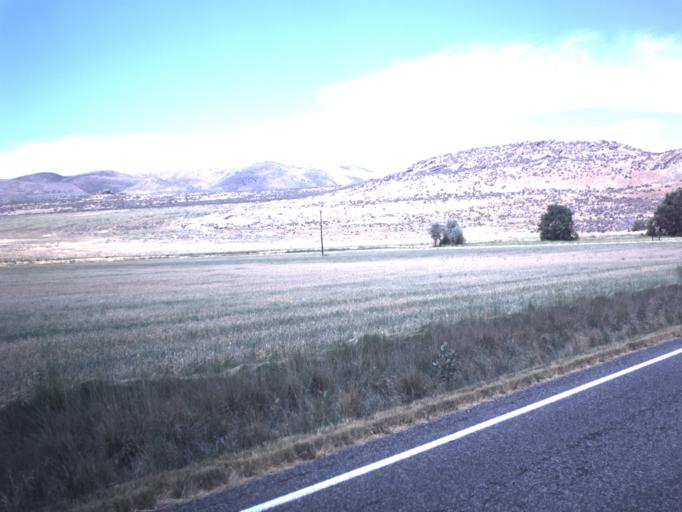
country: US
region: Utah
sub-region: Box Elder County
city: Tremonton
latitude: 41.6313
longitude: -112.3308
